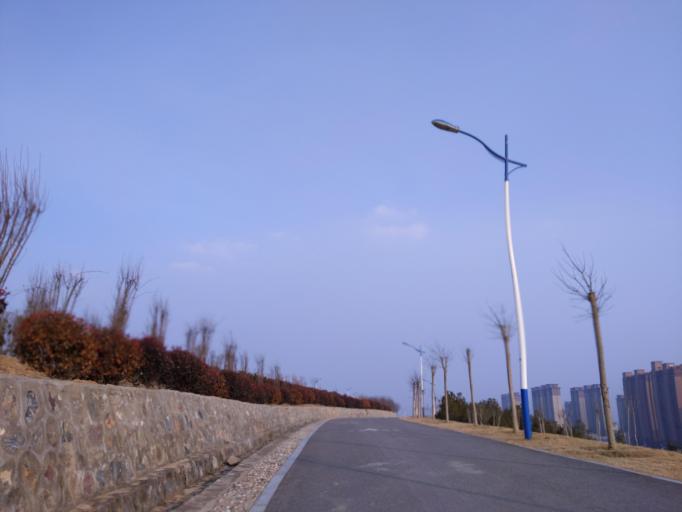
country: CN
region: Henan Sheng
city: Puyang
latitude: 35.8193
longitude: 115.0137
